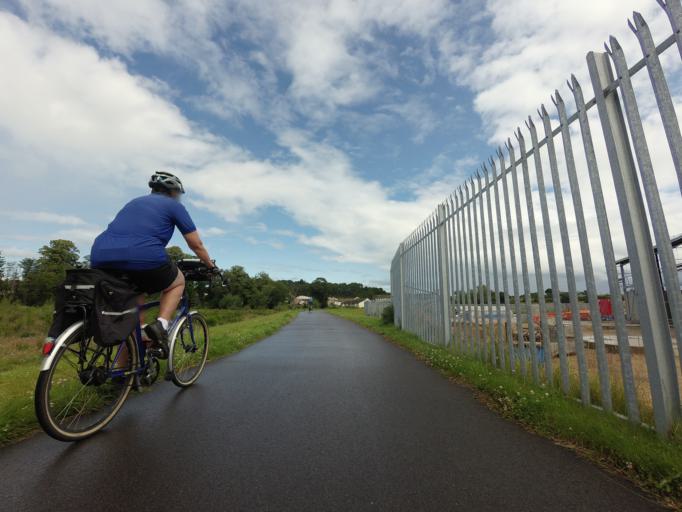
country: GB
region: Scotland
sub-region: Moray
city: Elgin
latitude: 57.6511
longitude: -3.2964
